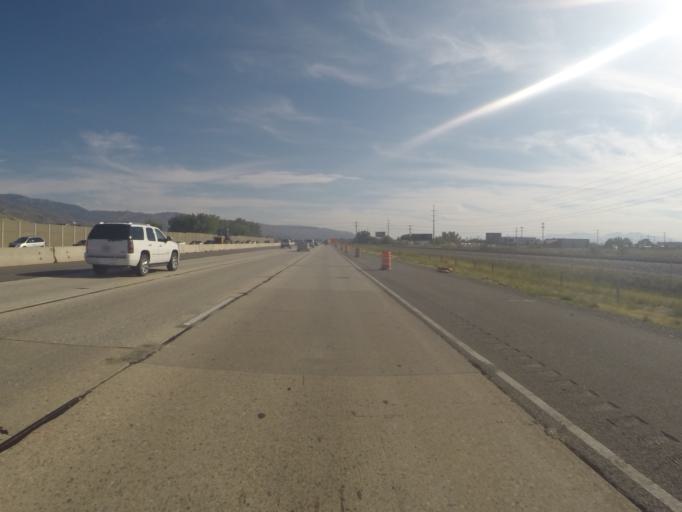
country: US
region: Utah
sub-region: Davis County
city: Centerville
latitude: 40.9313
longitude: -111.8916
